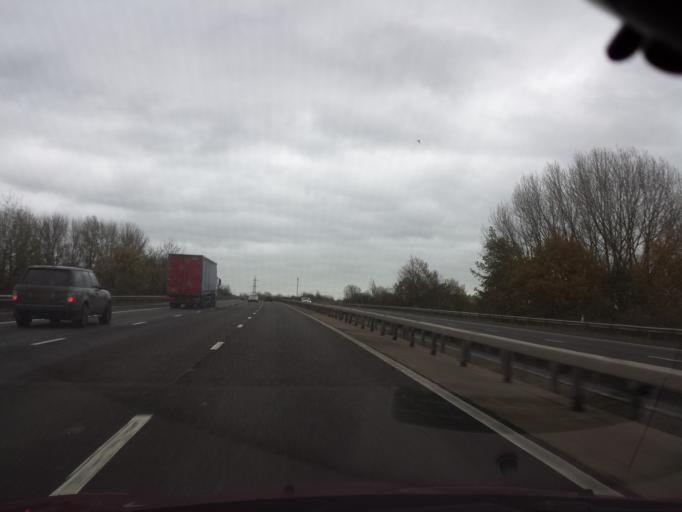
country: GB
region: England
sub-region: Surrey
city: Chertsey
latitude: 51.3945
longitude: -0.4899
